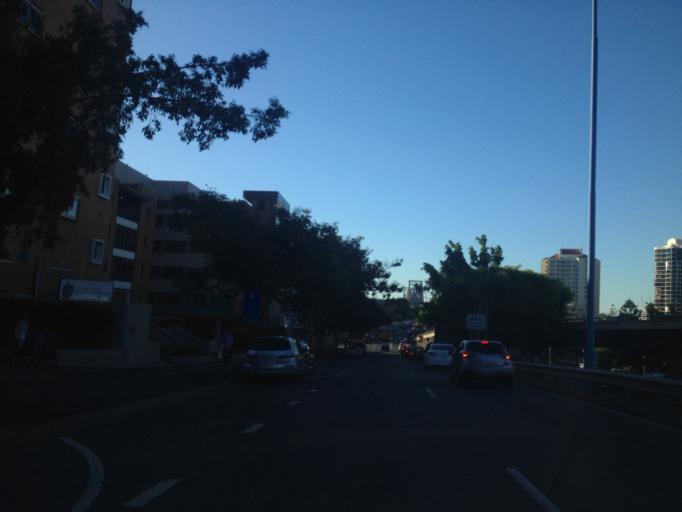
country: AU
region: Queensland
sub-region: Brisbane
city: Brisbane
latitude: -27.4745
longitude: 153.0356
